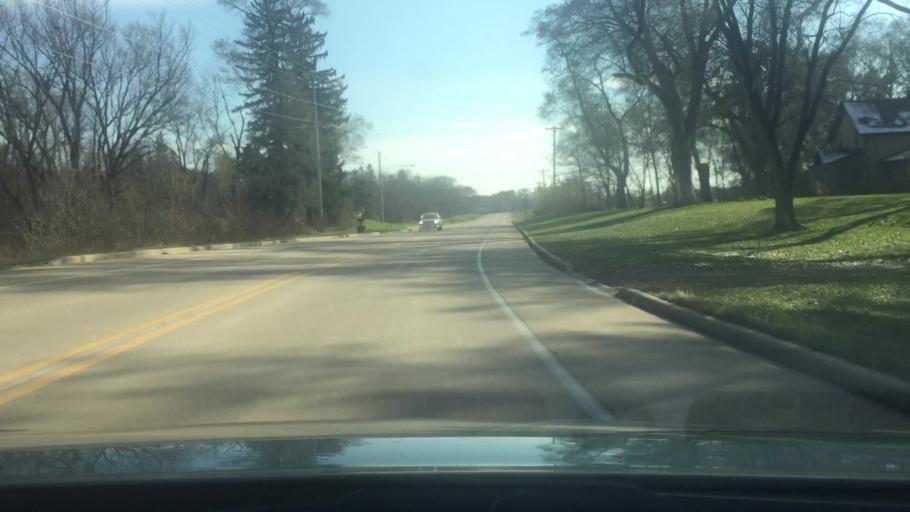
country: US
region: Wisconsin
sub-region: Jefferson County
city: Cambridge
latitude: 42.9979
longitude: -89.0020
